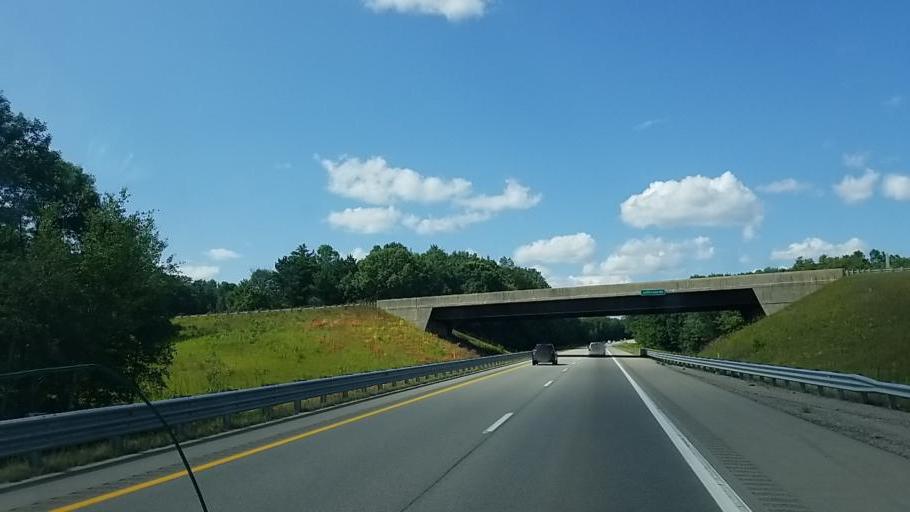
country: US
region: Michigan
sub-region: Montcalm County
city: Howard City
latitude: 43.4890
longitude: -85.4835
